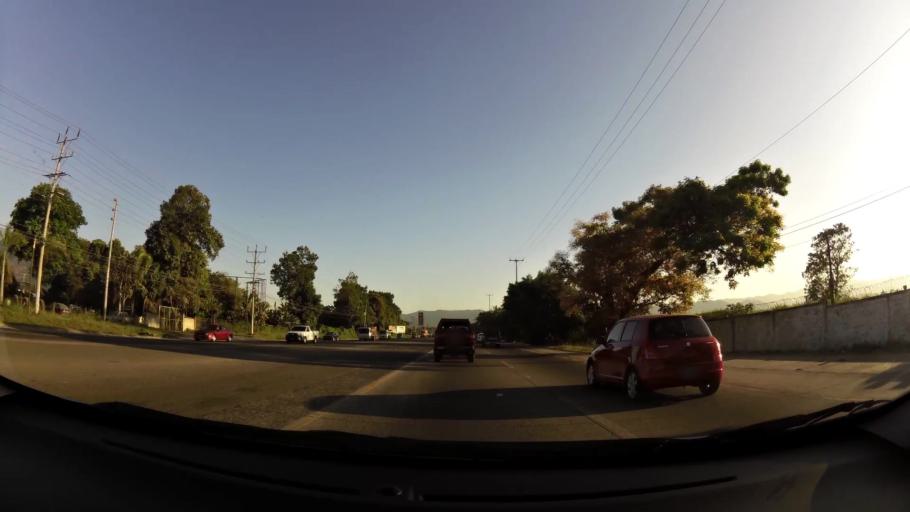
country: SV
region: La Libertad
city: Ciudad Arce
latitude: 13.7683
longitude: -89.3705
